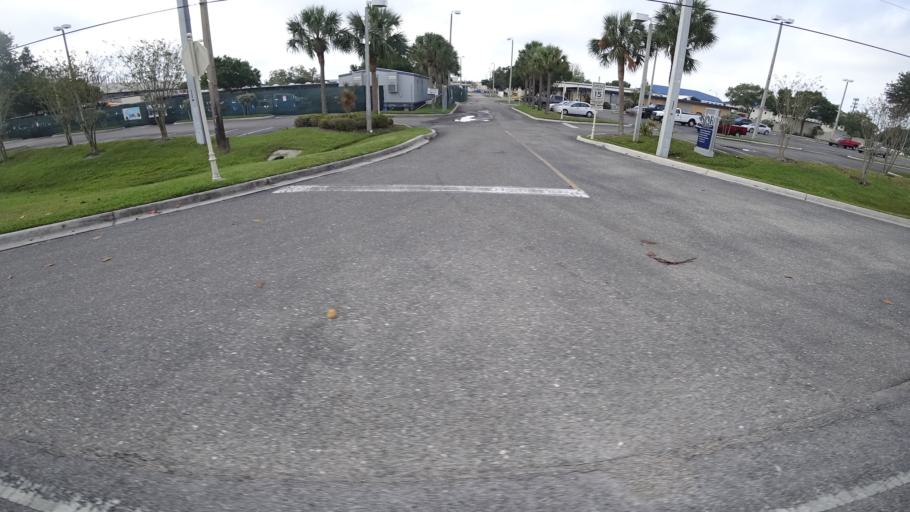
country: US
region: Florida
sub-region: Manatee County
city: Bayshore Gardens
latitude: 27.4404
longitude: -82.5915
